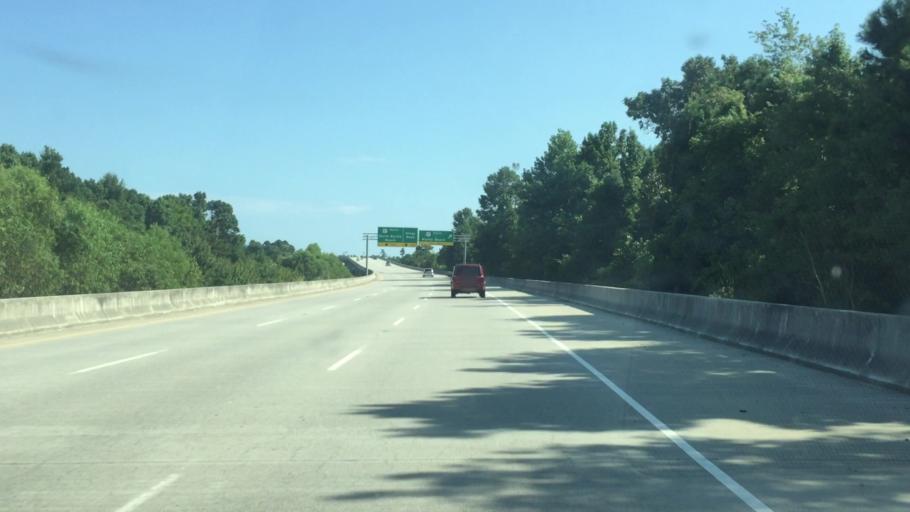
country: US
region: South Carolina
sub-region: Horry County
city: North Myrtle Beach
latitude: 33.7968
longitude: -78.7794
